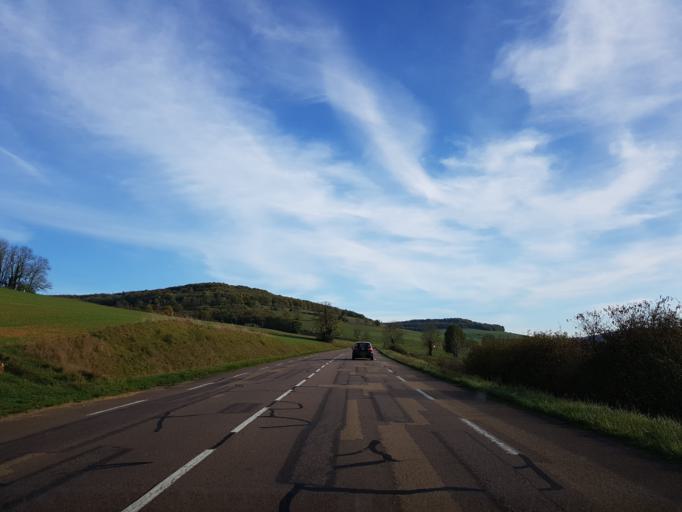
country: FR
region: Bourgogne
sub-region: Departement de la Cote-d'Or
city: Vitteaux
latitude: 47.3574
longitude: 4.5699
